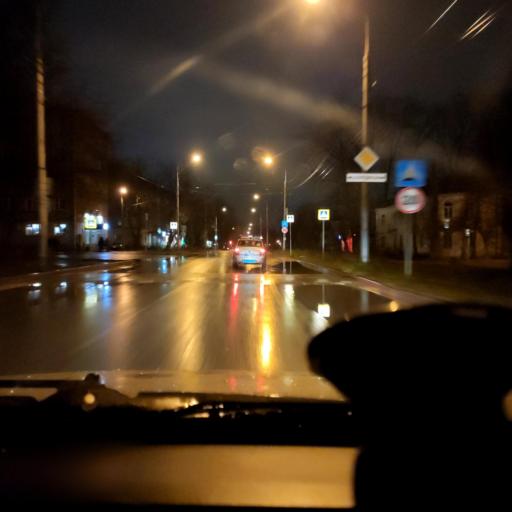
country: RU
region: Perm
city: Perm
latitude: 57.9666
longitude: 56.2294
